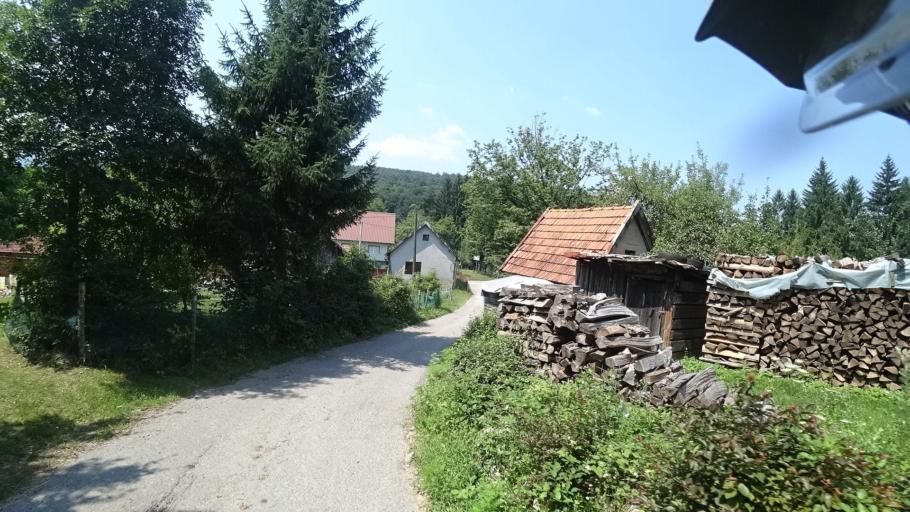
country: HR
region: Karlovacka
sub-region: Grad Ogulin
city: Ogulin
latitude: 45.3040
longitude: 15.1799
